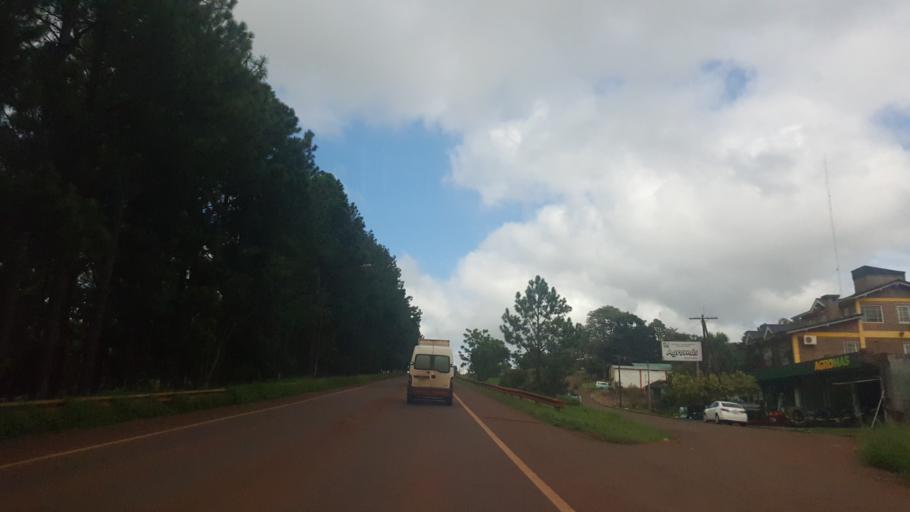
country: AR
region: Misiones
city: Aristobulo del Valle
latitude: -27.0847
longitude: -54.8260
